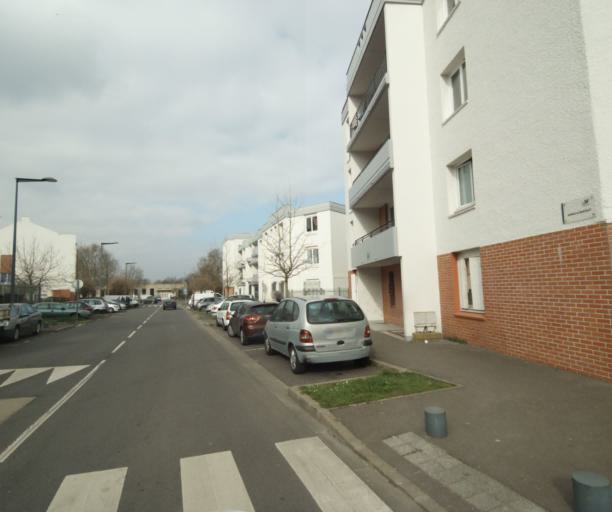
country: FR
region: Ile-de-France
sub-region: Departement du Val-d'Oise
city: Vaureal
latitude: 49.0500
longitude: 2.0399
